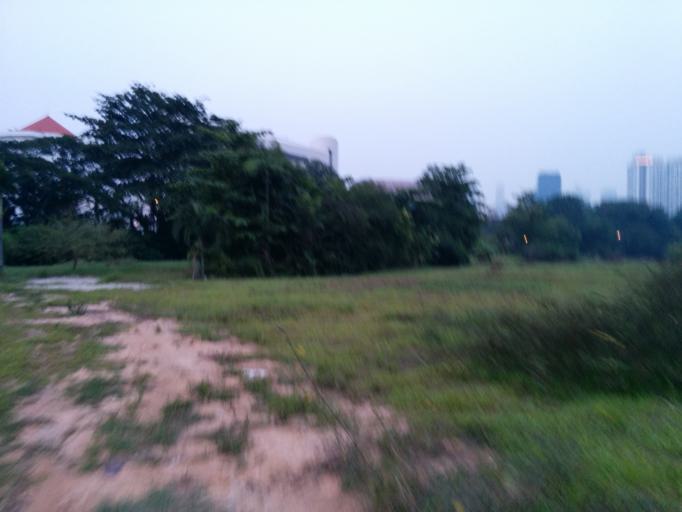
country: SG
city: Singapore
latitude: 1.2755
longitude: 103.8317
